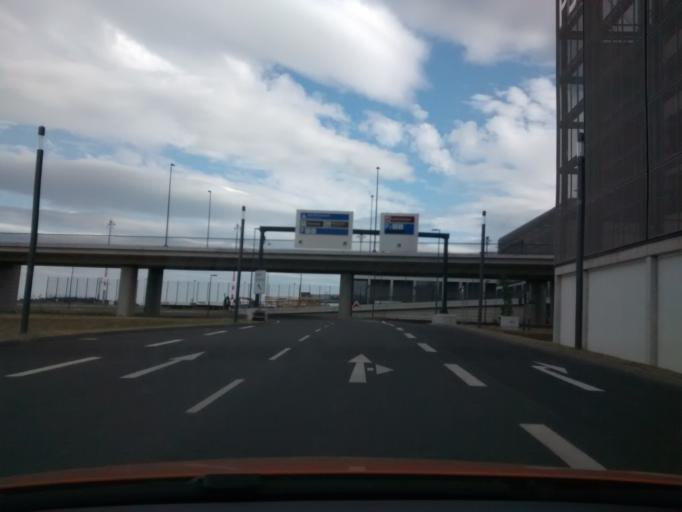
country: DE
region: Brandenburg
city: Schonefeld
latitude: 52.3638
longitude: 13.5136
